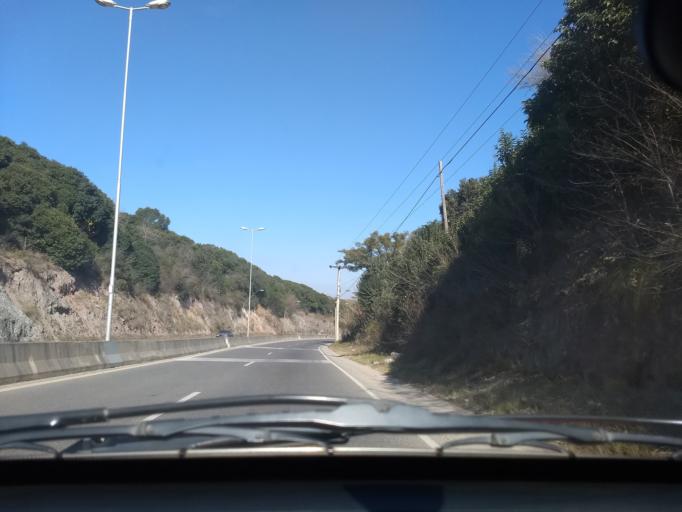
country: AR
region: Cordoba
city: Rio Ceballos
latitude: -31.1588
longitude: -64.3011
